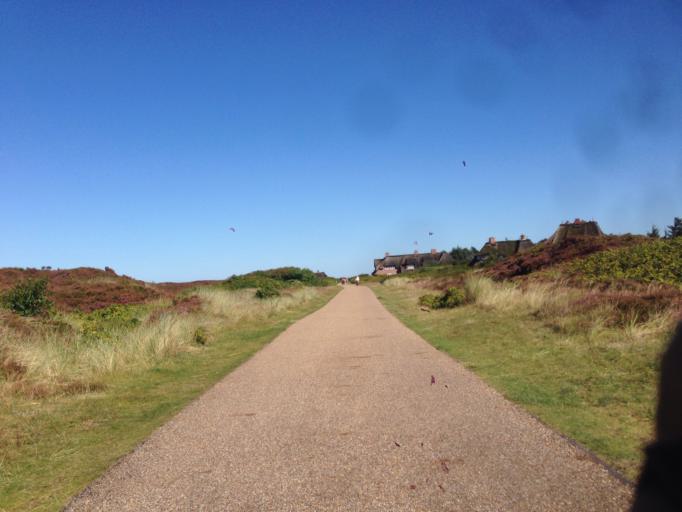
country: DE
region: Schleswig-Holstein
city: Tinnum
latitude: 54.9523
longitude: 8.3371
